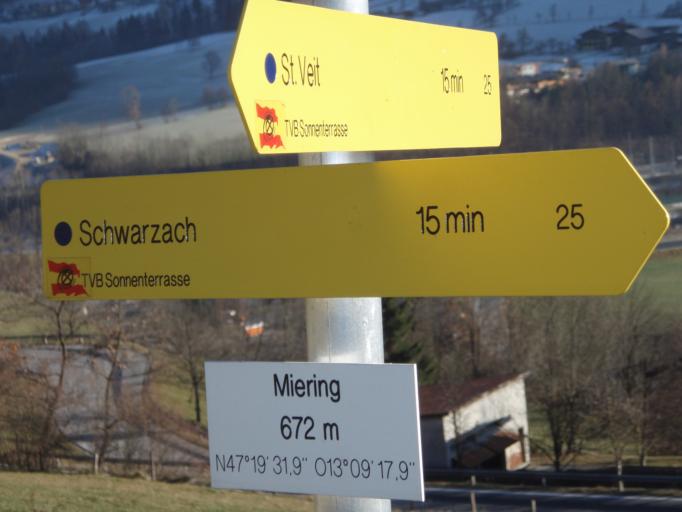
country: AT
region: Salzburg
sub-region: Politischer Bezirk Sankt Johann im Pongau
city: Schwarzach im Pongau
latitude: 47.3255
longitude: 13.1542
